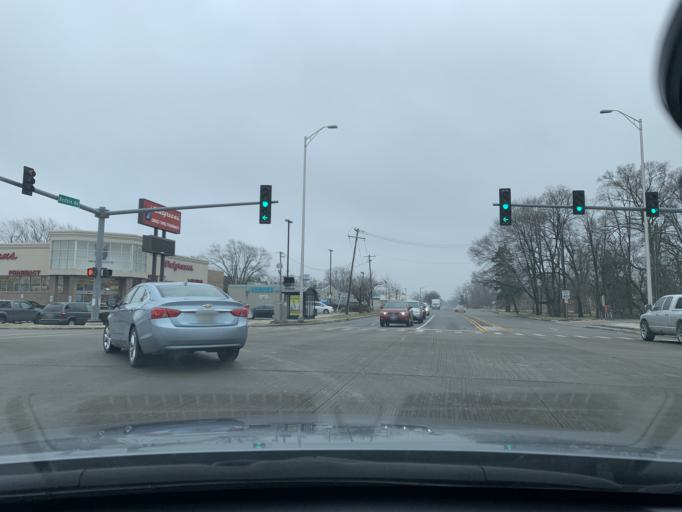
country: US
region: Illinois
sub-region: Cook County
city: Posen
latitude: 41.6260
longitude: -87.6984
